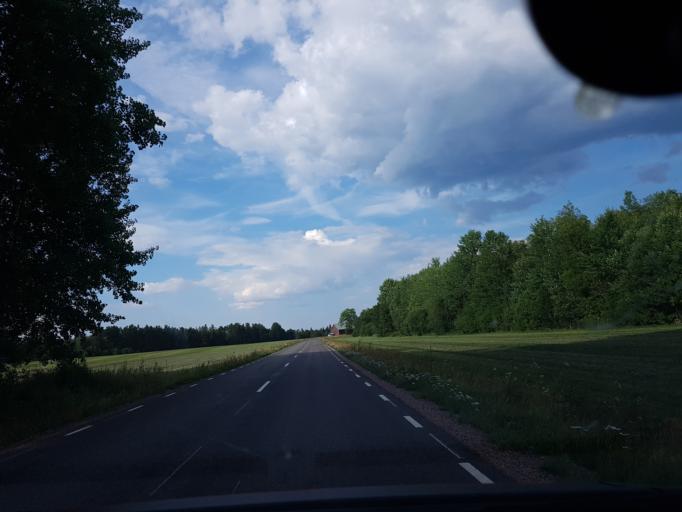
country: SE
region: Joenkoeping
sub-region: Gislaveds Kommun
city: Reftele
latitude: 57.2035
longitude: 13.5986
